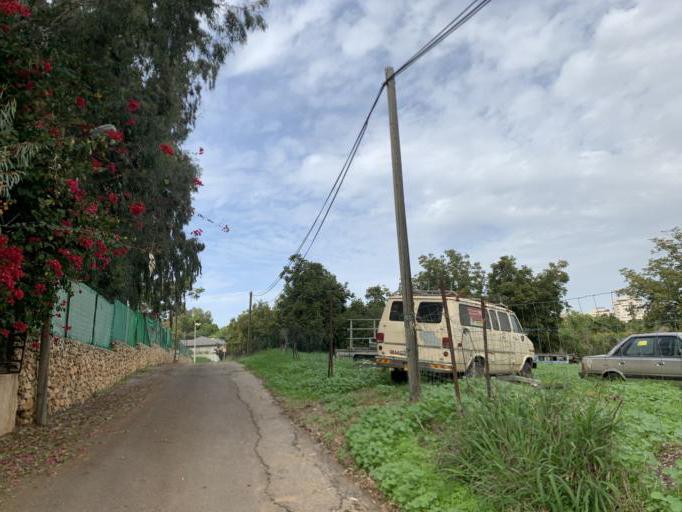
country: IL
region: Central District
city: Hod HaSharon
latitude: 32.1535
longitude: 34.9014
